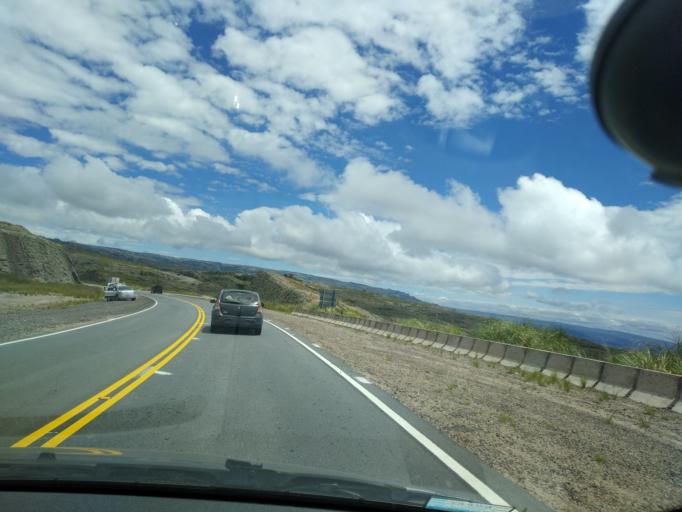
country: AR
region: Cordoba
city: Cuesta Blanca
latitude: -31.6095
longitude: -64.7140
